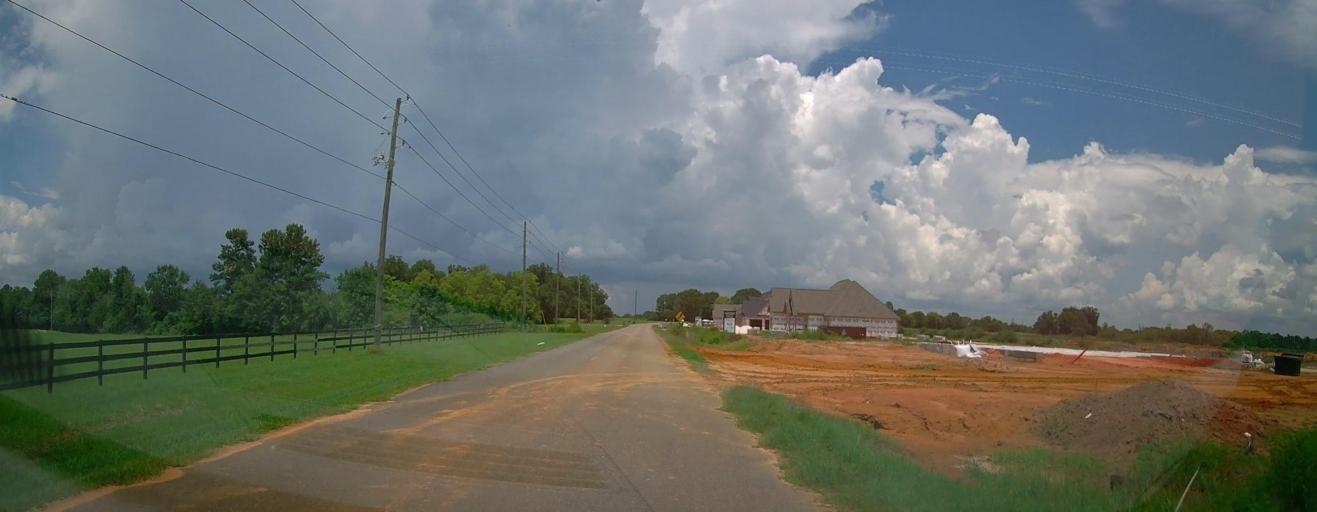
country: US
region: Georgia
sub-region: Houston County
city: Perry
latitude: 32.4940
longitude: -83.6422
